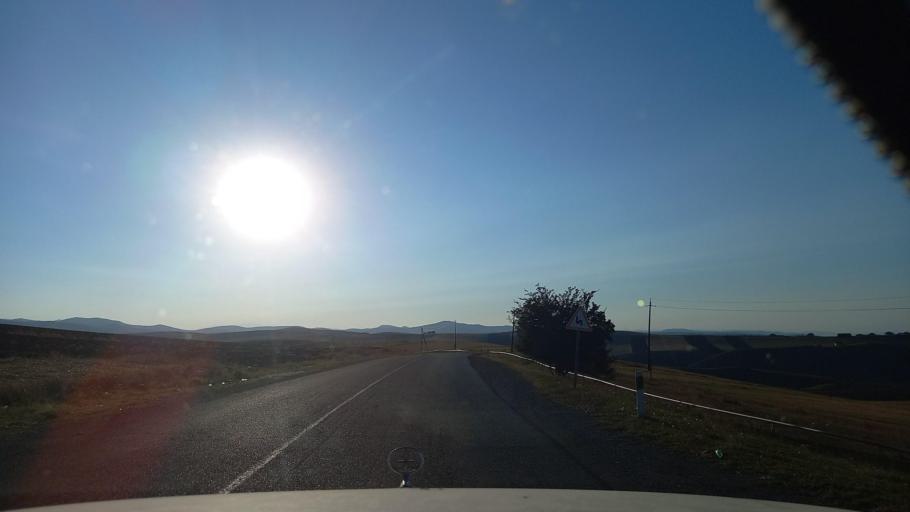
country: AZ
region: Shamkir Rayon
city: Shamkhor
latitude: 40.7658
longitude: 45.9398
